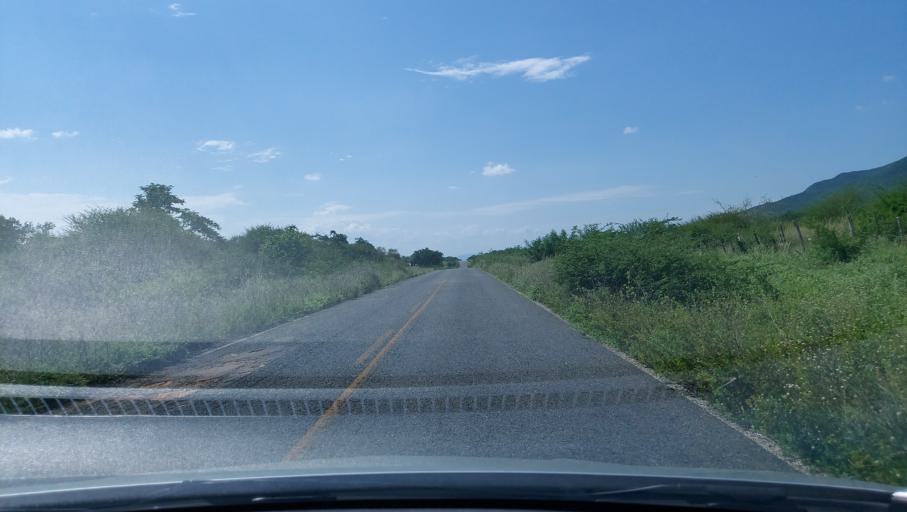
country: BR
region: Bahia
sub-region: Oliveira Dos Brejinhos
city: Beira Rio
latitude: -12.1565
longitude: -42.5514
